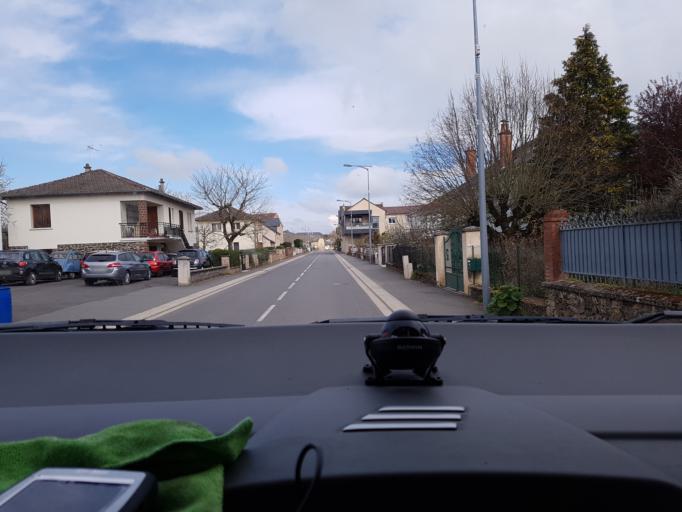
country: FR
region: Midi-Pyrenees
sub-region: Departement de l'Aveyron
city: Colombies
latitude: 44.4058
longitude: 2.2916
